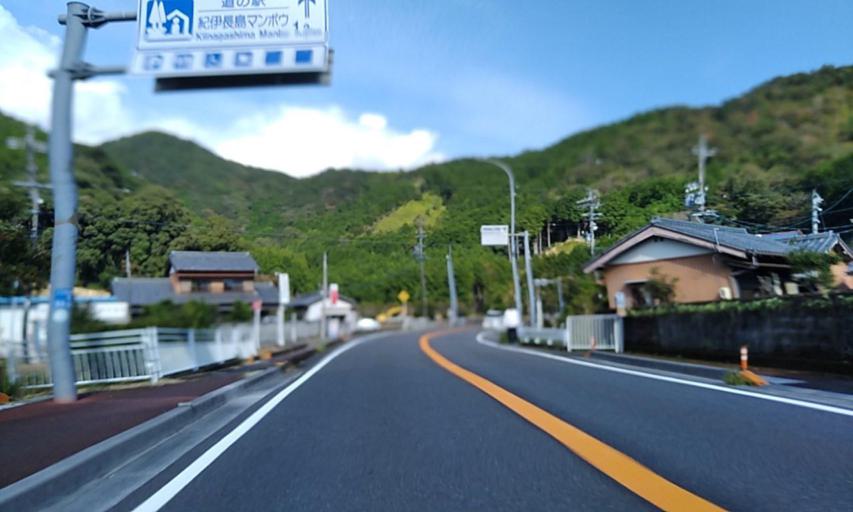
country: JP
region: Mie
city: Owase
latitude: 34.2132
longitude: 136.3358
